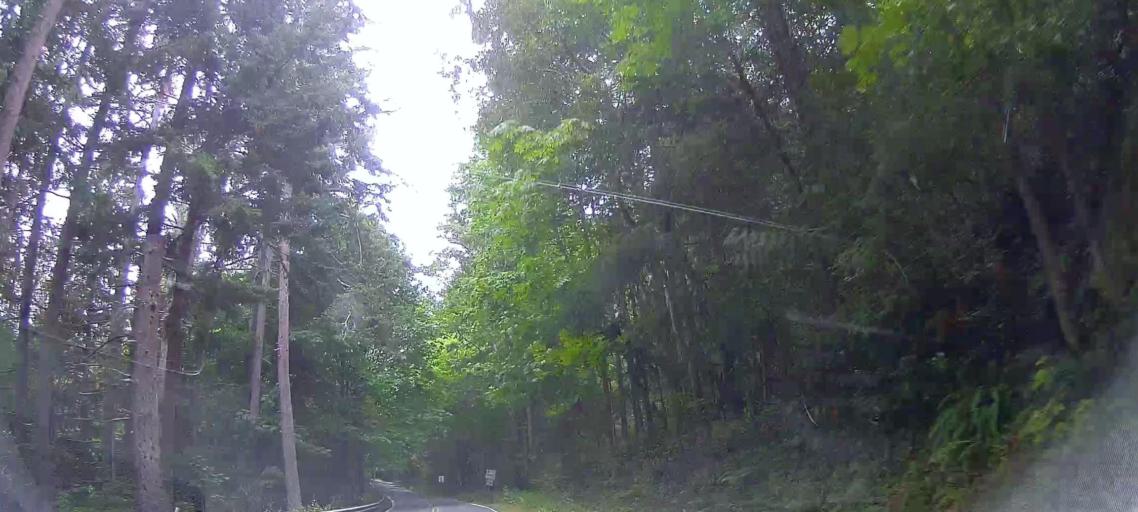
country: US
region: Washington
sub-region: Skagit County
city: Anacortes
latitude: 48.4544
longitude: -122.6341
